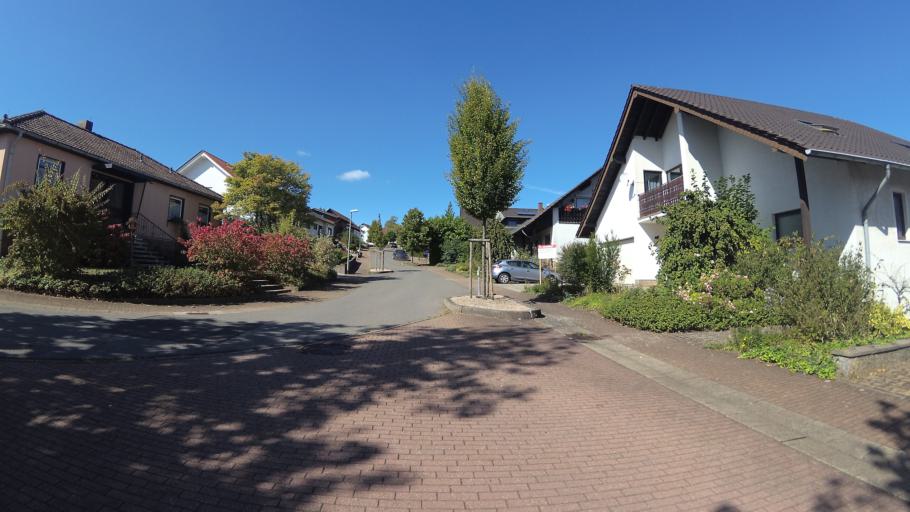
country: DE
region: Saarland
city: Lebach
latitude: 49.3891
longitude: 6.9010
